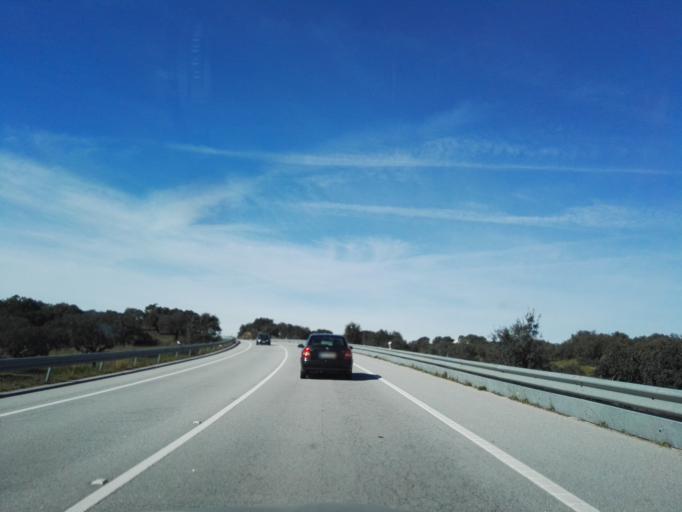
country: PT
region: Portalegre
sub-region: Portalegre
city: Alegrete
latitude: 39.1863
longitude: -7.3473
